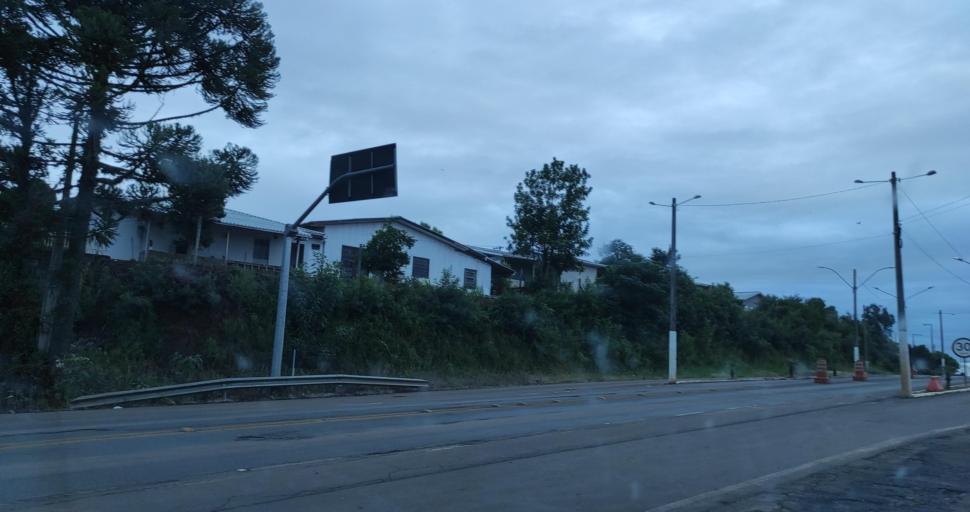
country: BR
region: Santa Catarina
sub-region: Xanxere
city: Xanxere
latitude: -26.7348
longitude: -52.3900
